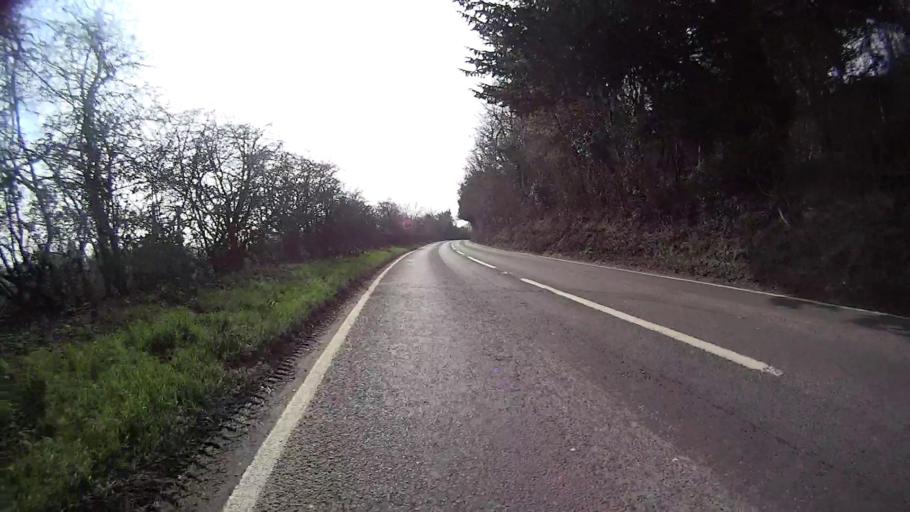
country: GB
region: England
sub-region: Surrey
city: Headley
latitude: 51.2542
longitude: -0.2627
